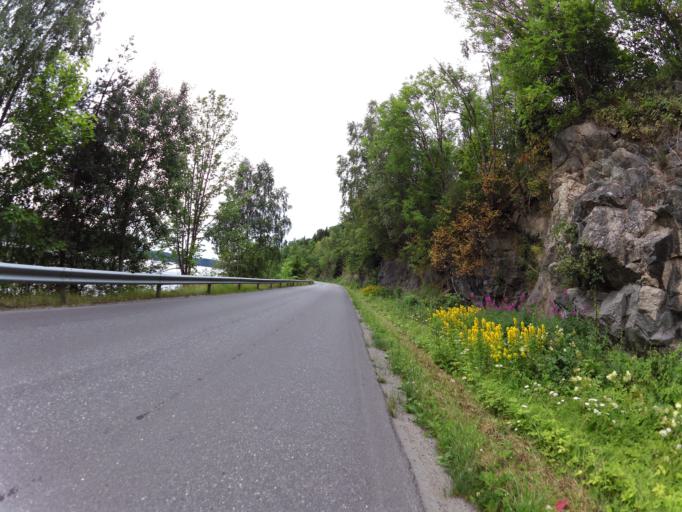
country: NO
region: Akershus
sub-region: As
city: As
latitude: 59.7001
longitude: 10.7374
